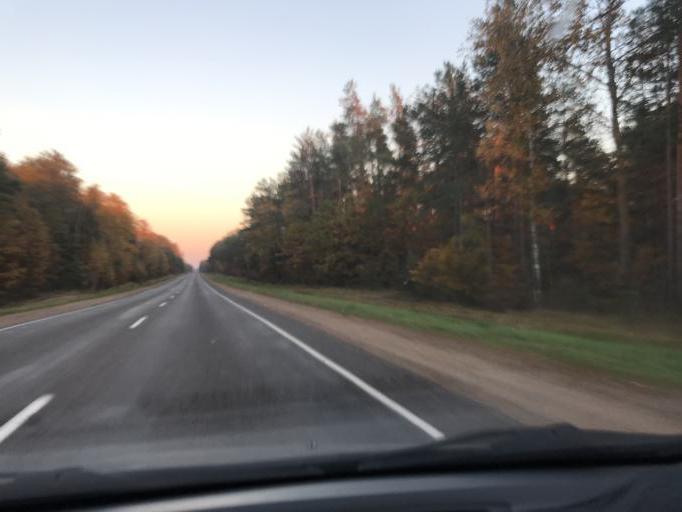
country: BY
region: Mogilev
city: Hlusha
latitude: 53.0938
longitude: 28.9502
